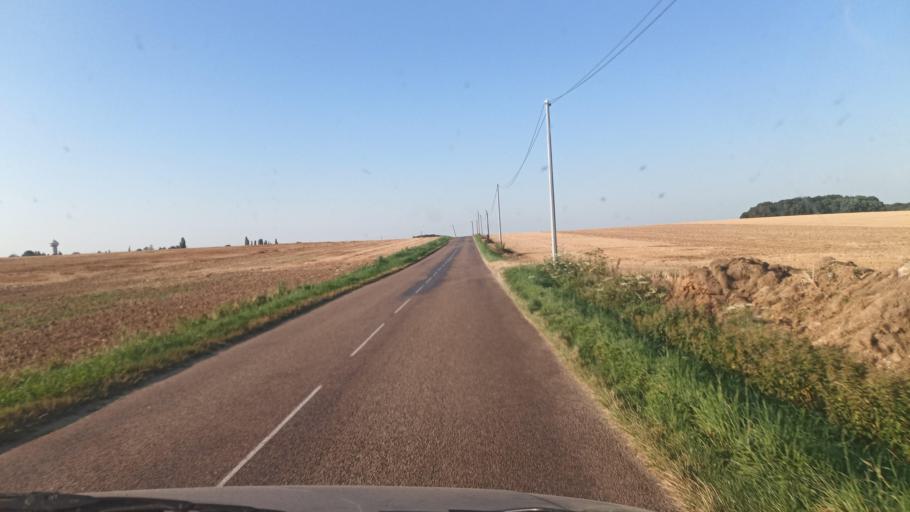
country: FR
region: Bourgogne
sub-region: Departement de l'Yonne
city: Saint-Valerien
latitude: 48.2010
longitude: 3.1178
